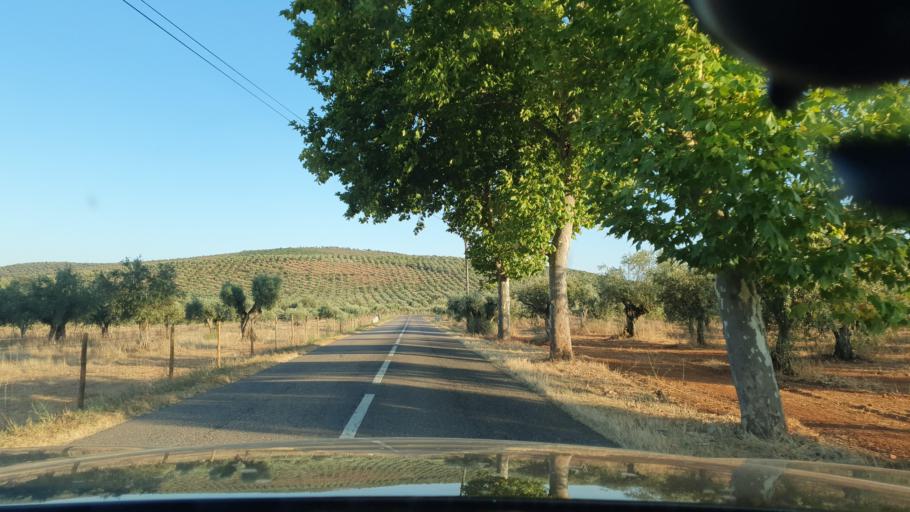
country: PT
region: Evora
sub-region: Estremoz
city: Estremoz
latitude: 38.9313
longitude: -7.6669
